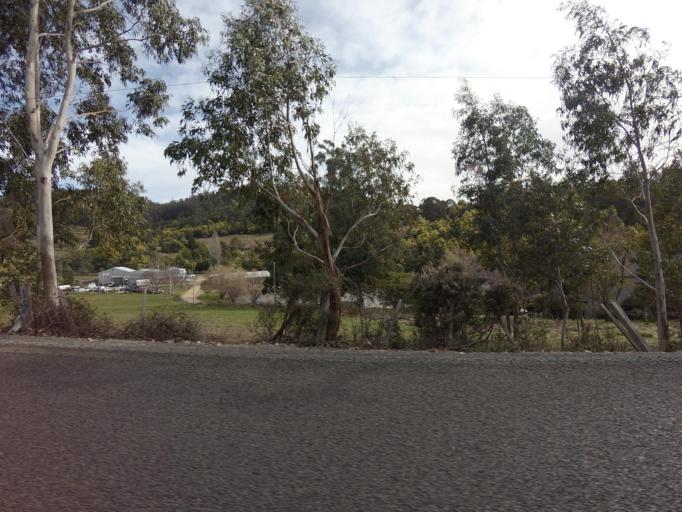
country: AU
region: Tasmania
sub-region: Kingborough
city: Margate
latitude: -42.9917
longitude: 147.1864
